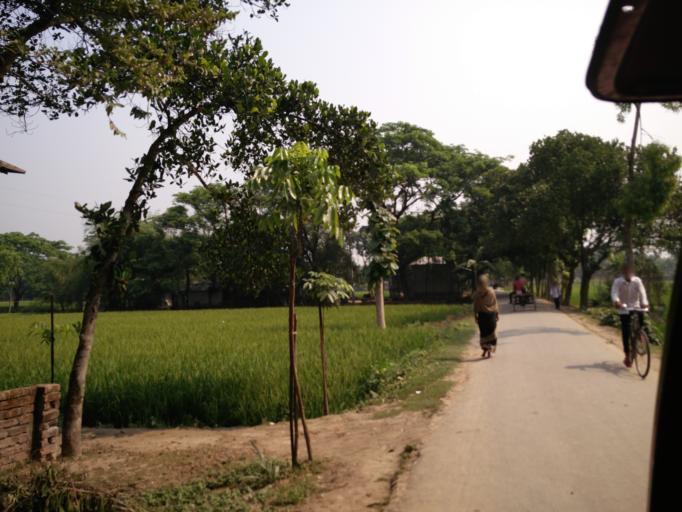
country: BD
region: Dhaka
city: Muktagacha
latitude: 24.9173
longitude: 90.2333
